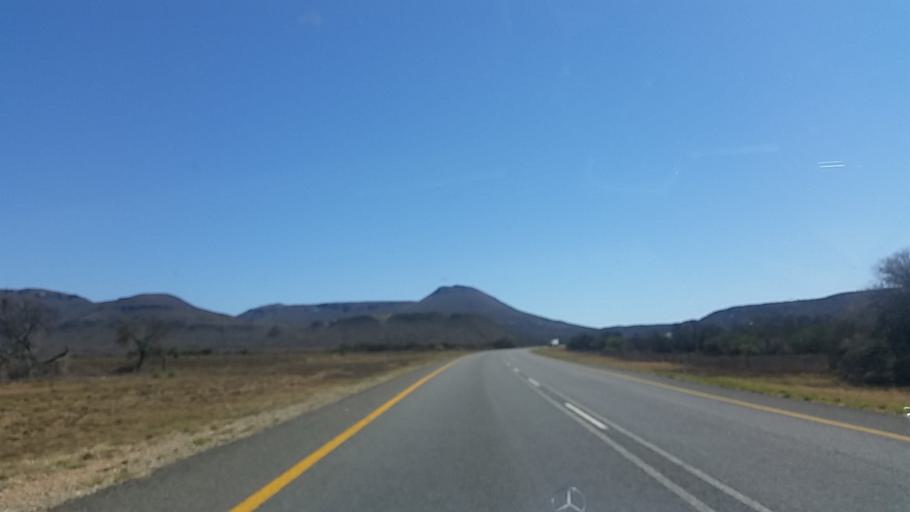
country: ZA
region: Eastern Cape
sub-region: Cacadu District Municipality
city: Graaff-Reinet
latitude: -32.0828
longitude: 24.6020
